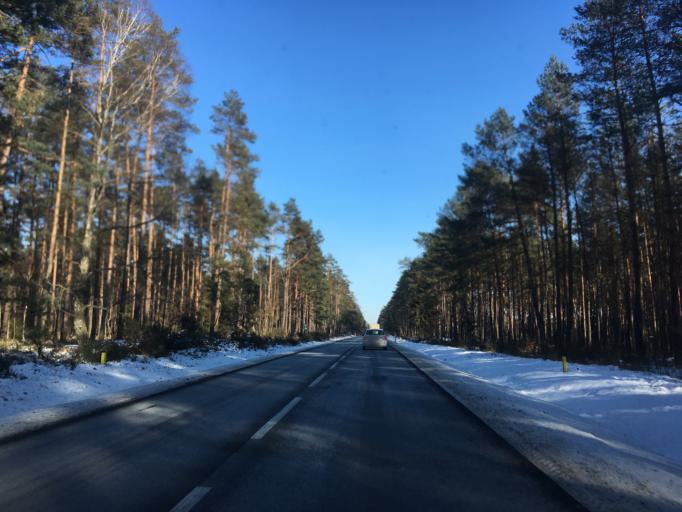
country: PL
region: Pomeranian Voivodeship
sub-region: Powiat koscierski
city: Lipusz
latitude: 54.1469
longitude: 17.7661
